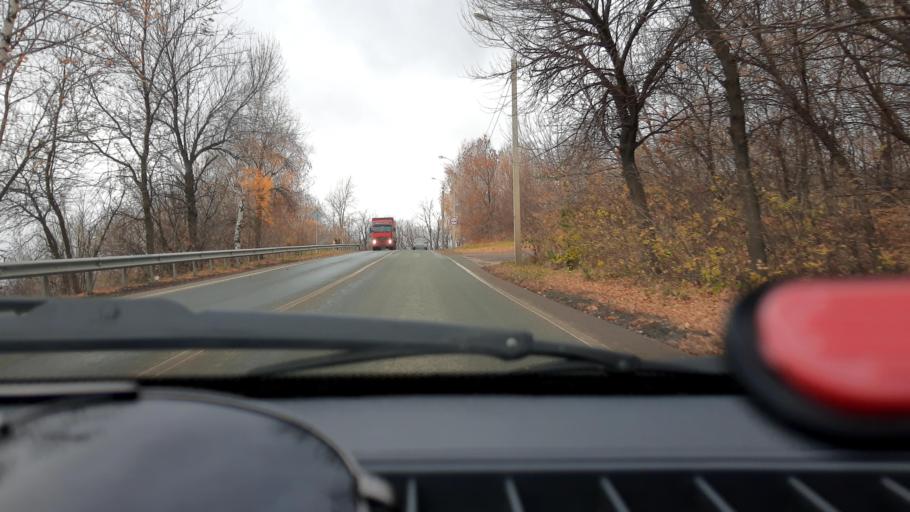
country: RU
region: Bashkortostan
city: Ufa
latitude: 54.8523
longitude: 56.0747
